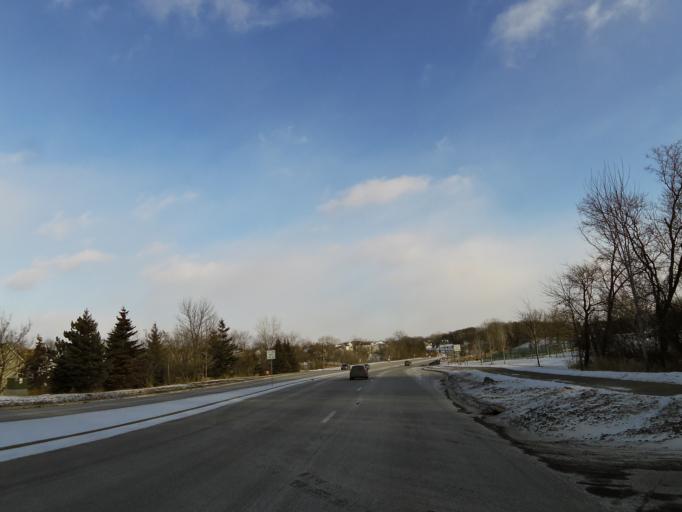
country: US
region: Minnesota
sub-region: Washington County
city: Woodbury
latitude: 44.9396
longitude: -92.9237
